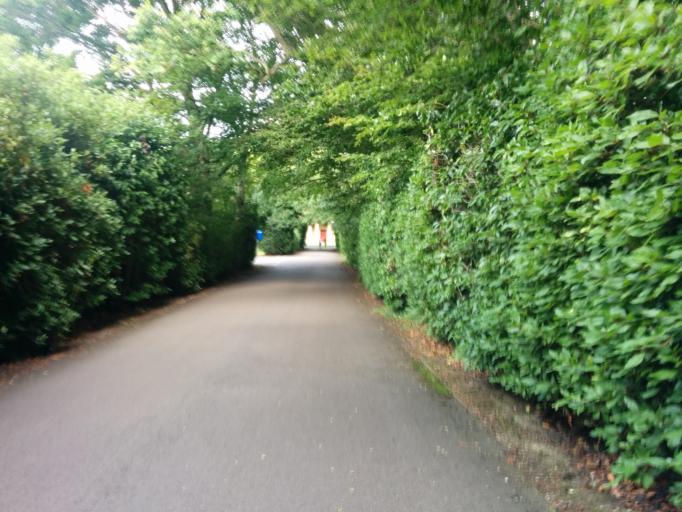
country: GB
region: England
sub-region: Cambridgeshire
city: Girton
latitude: 52.2132
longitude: 0.0954
